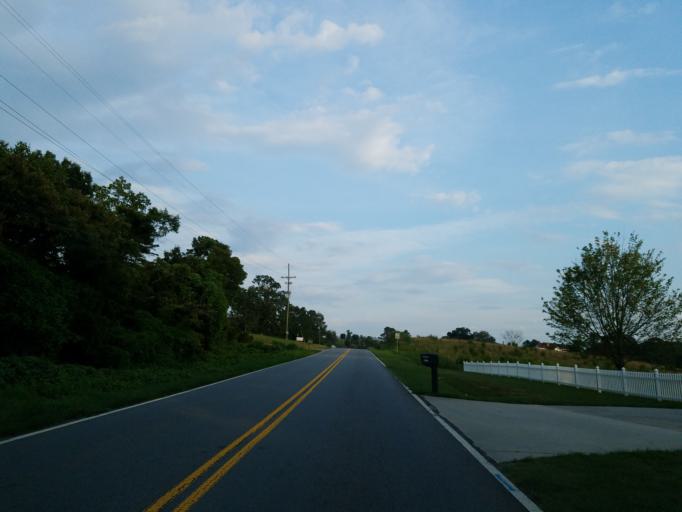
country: US
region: Georgia
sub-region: Gilmer County
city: Ellijay
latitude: 34.6549
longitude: -84.4720
